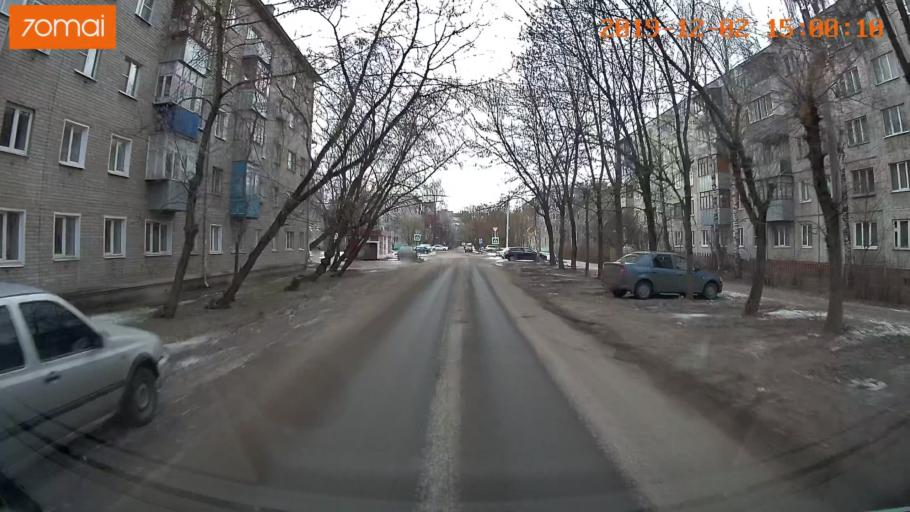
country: RU
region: Ivanovo
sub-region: Gorod Ivanovo
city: Ivanovo
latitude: 56.9701
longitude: 41.0056
